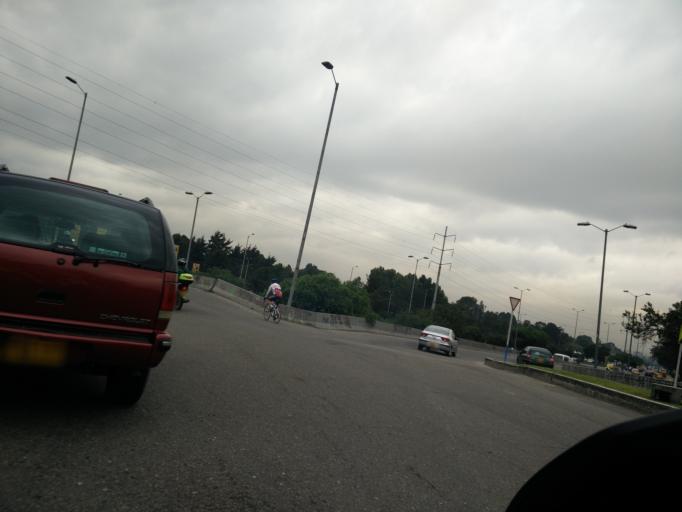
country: CO
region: Bogota D.C.
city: Bogota
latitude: 4.6661
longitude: -74.0938
